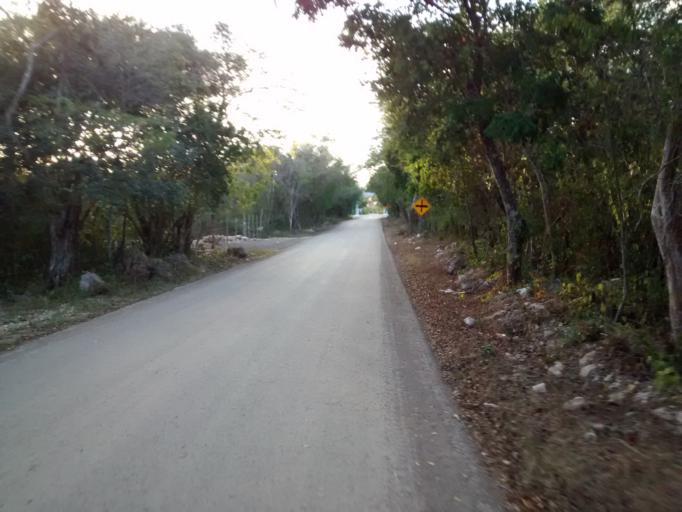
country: MX
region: Yucatan
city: Valladolid
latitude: 20.6812
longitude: -88.1634
